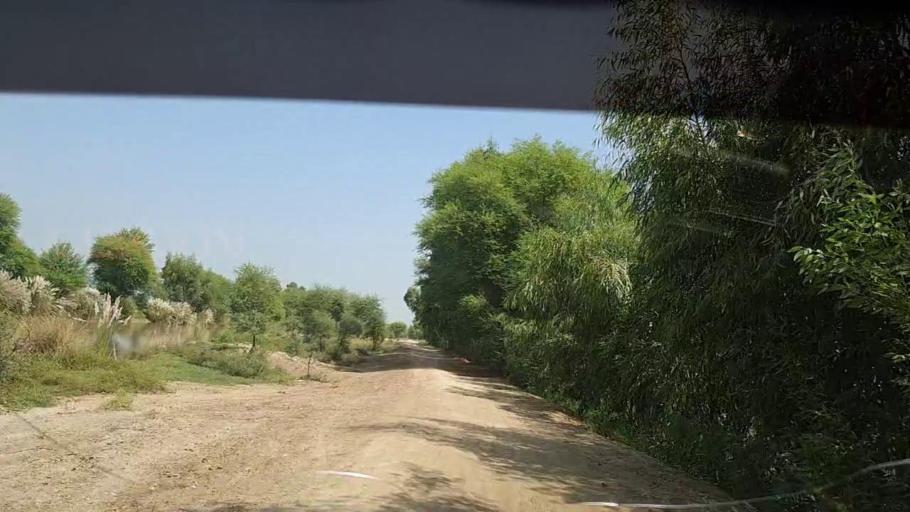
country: PK
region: Sindh
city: Tangwani
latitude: 28.2328
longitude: 68.9547
